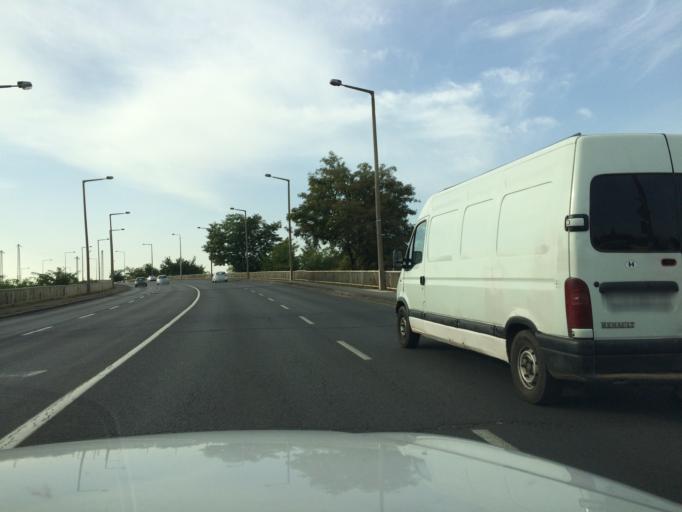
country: HU
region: Szabolcs-Szatmar-Bereg
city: Nyiregyhaza
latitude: 47.9574
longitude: 21.7001
